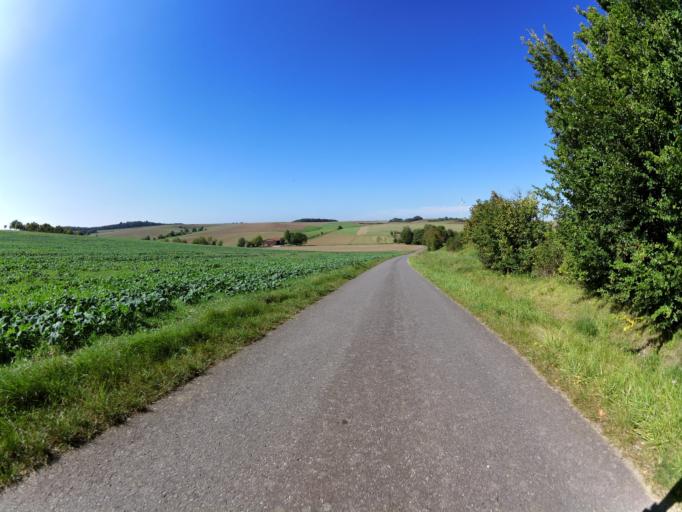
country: DE
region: Baden-Wuerttemberg
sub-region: Regierungsbezirk Stuttgart
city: Grossrinderfeld
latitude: 49.6979
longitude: 9.7837
